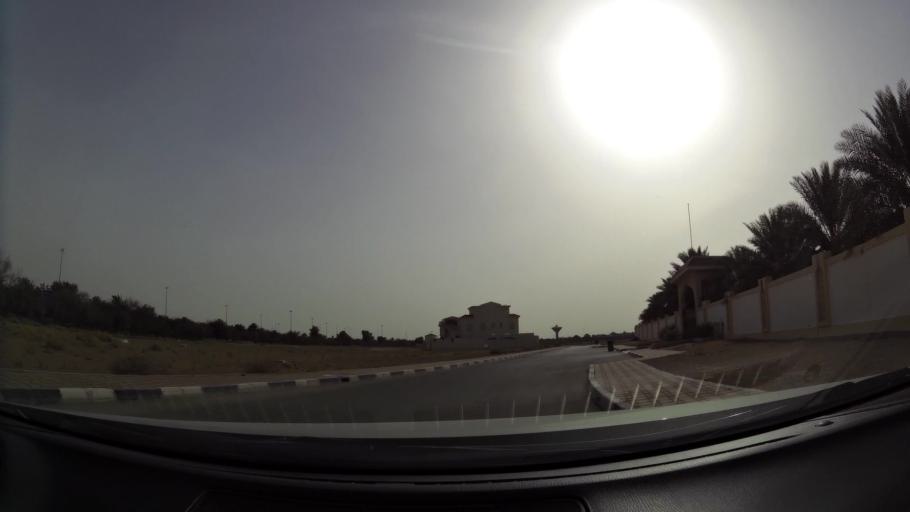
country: AE
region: Abu Dhabi
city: Al Ain
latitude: 24.1887
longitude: 55.6050
